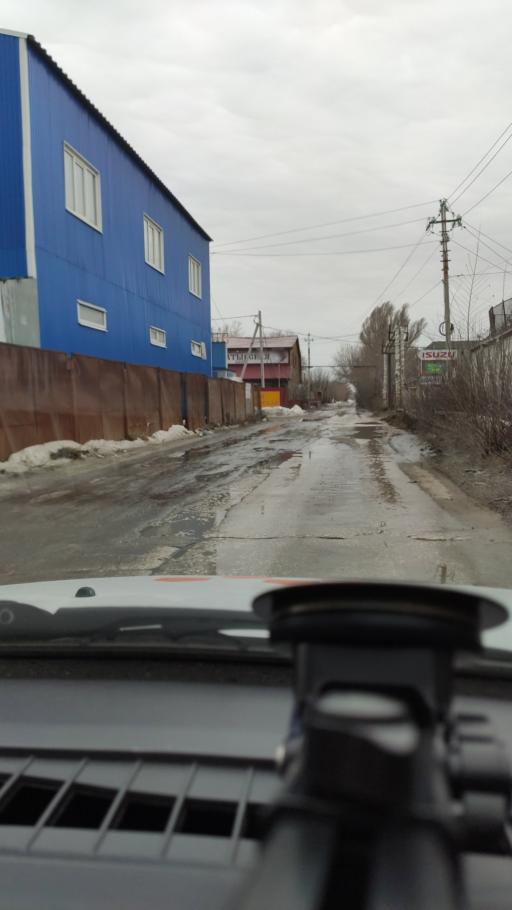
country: RU
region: Samara
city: Tol'yatti
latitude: 53.5364
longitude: 49.2593
